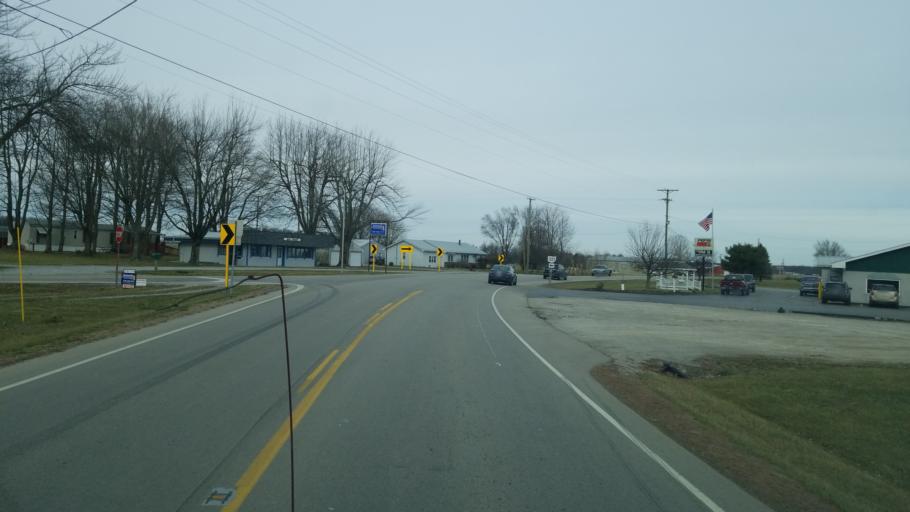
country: US
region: Ohio
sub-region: Adams County
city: Winchester
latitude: 39.0623
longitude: -83.7036
